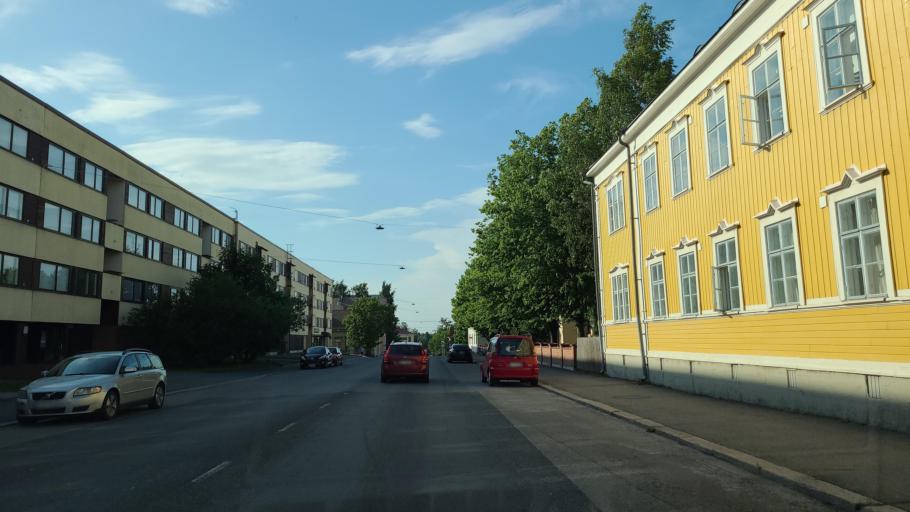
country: FI
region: Ostrobothnia
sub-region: Vaasa
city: Vaasa
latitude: 63.1024
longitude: 21.6200
